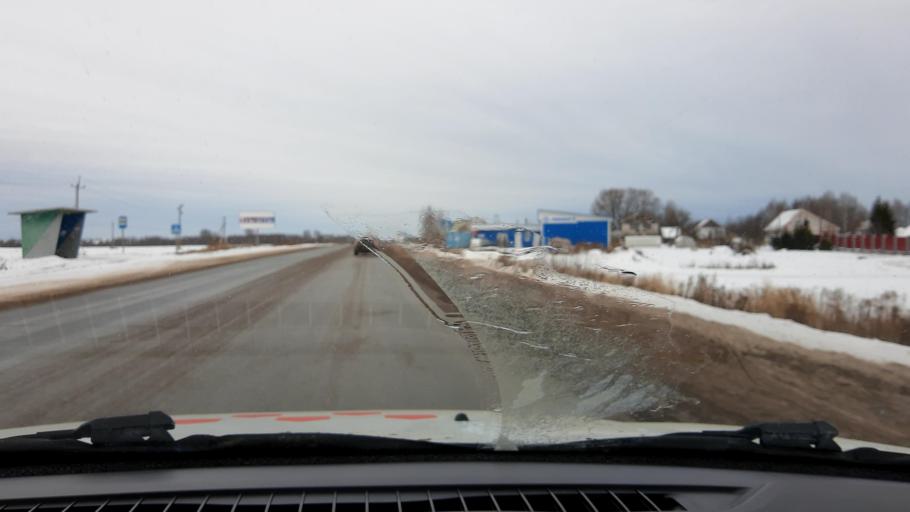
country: RU
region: Nizjnij Novgorod
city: Gorodets
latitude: 56.6514
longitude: 43.5080
